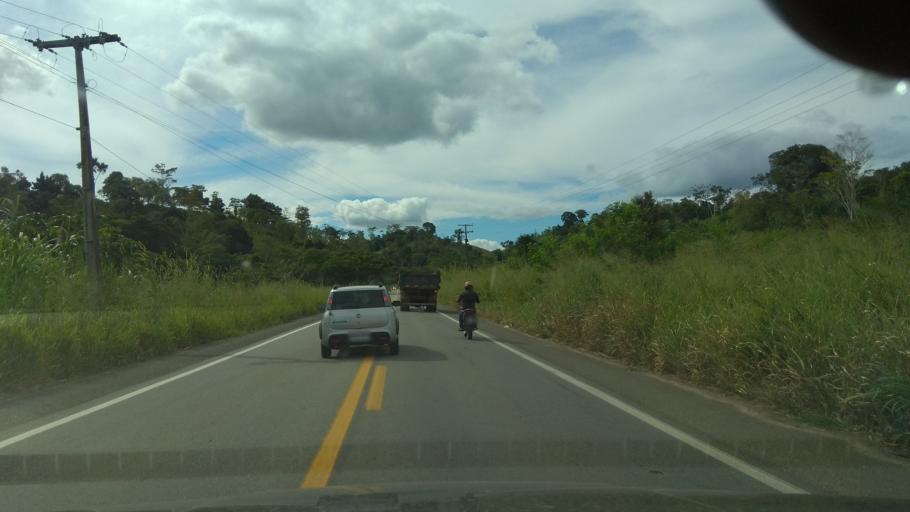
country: BR
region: Bahia
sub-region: Ipiau
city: Ipiau
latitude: -14.1023
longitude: -39.7774
